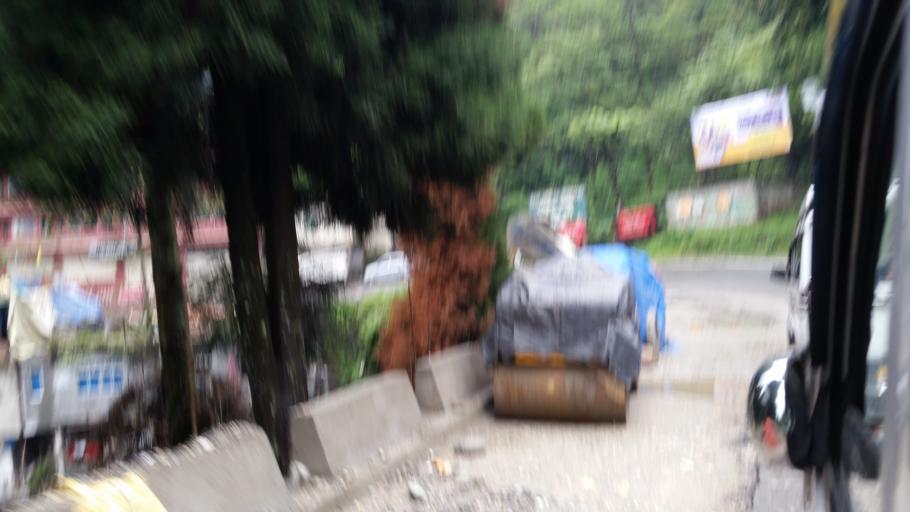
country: IN
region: West Bengal
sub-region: Darjiling
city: Darjiling
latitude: 27.0195
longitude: 88.2527
